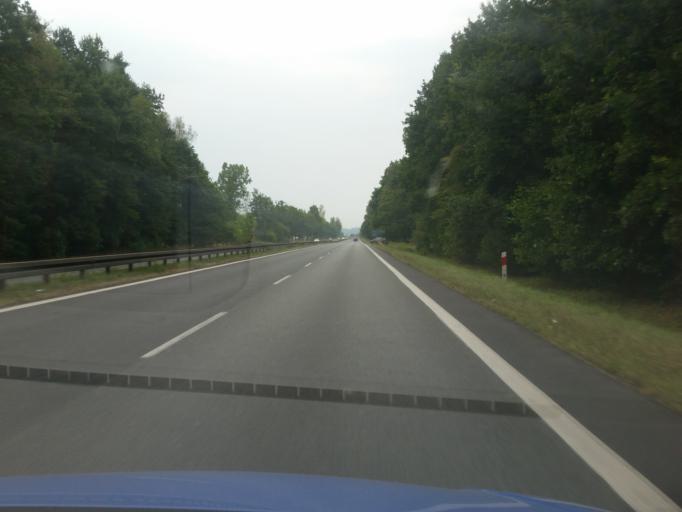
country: PL
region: Silesian Voivodeship
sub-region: Powiat bedzinski
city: Sarnow
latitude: 50.3898
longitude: 19.1846
